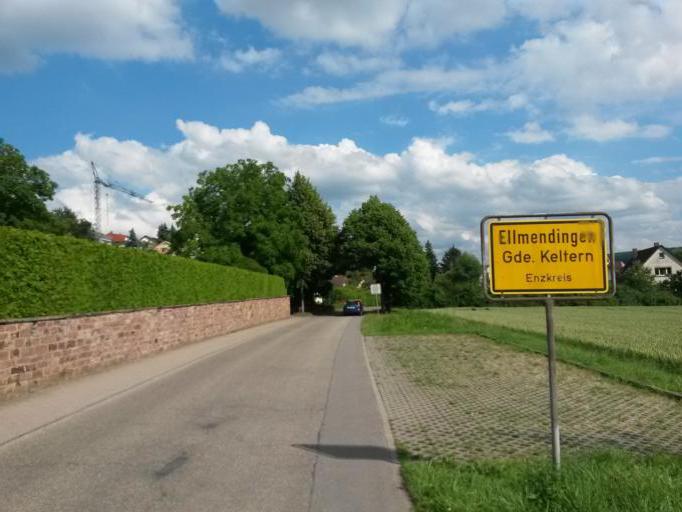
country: DE
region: Baden-Wuerttemberg
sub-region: Karlsruhe Region
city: Neuenburg
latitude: 48.9057
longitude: 8.5719
